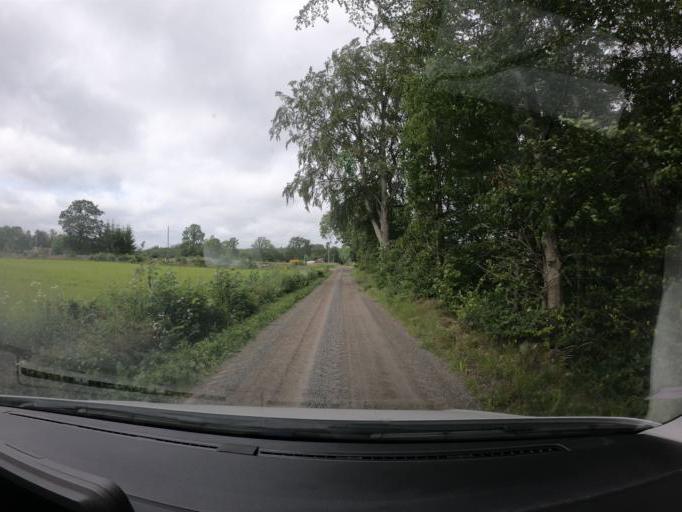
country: SE
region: Skane
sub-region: Perstorps Kommun
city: Perstorp
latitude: 56.1883
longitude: 13.5189
